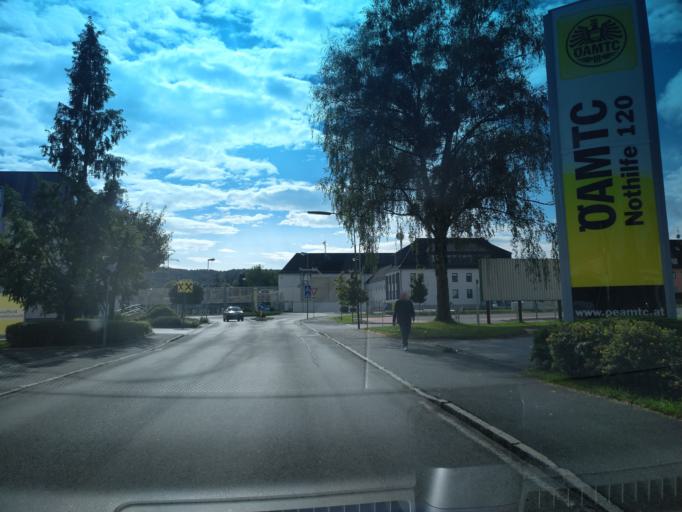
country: AT
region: Styria
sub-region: Politischer Bezirk Deutschlandsberg
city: Deutschlandsberg
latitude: 46.8195
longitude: 15.2257
